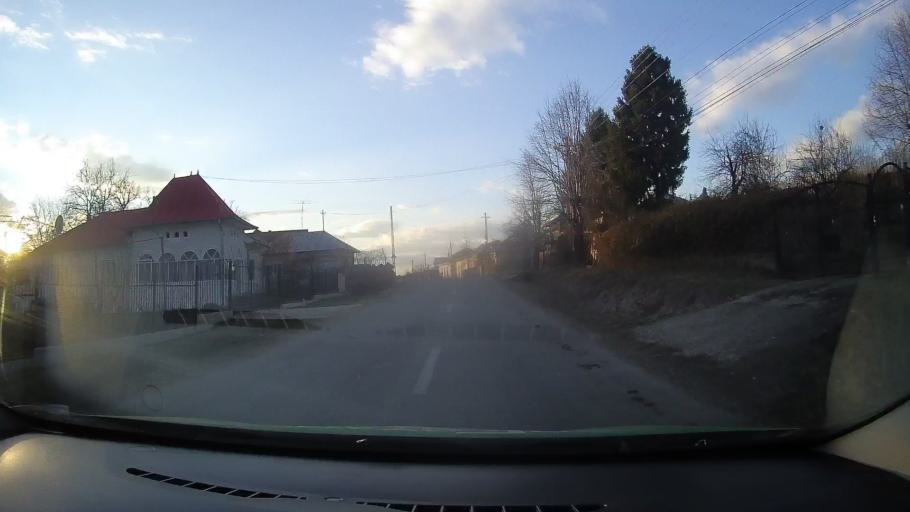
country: RO
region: Dambovita
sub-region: Comuna Gura Ocnitei
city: Adanca
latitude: 44.9200
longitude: 25.6153
